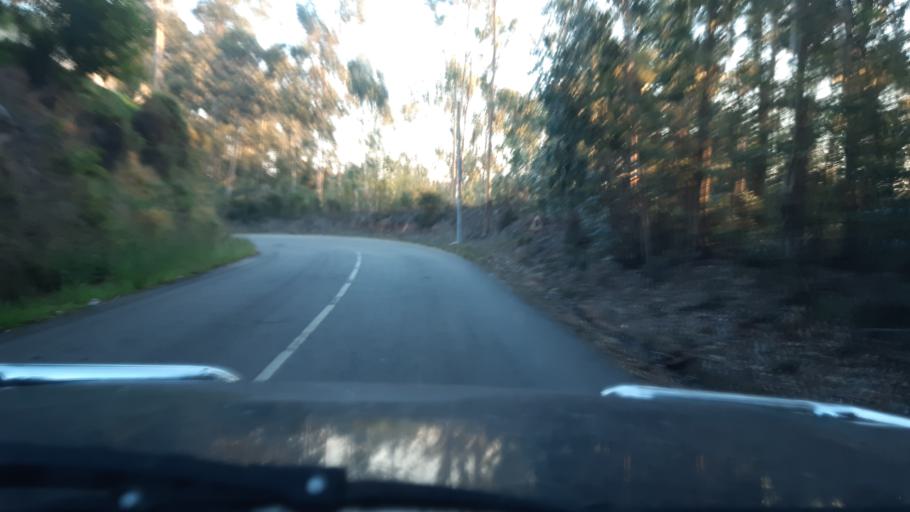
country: PT
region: Aveiro
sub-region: Agueda
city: Agueda
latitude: 40.5788
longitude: -8.4633
